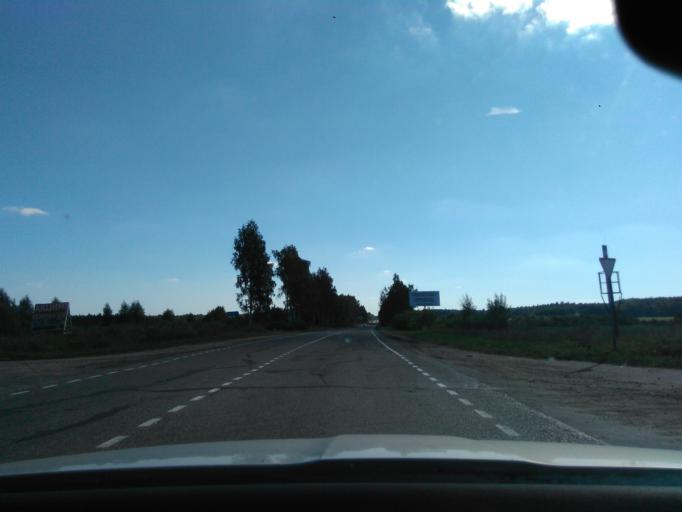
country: RU
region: Tverskaya
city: Konakovo
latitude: 56.6370
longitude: 36.7001
